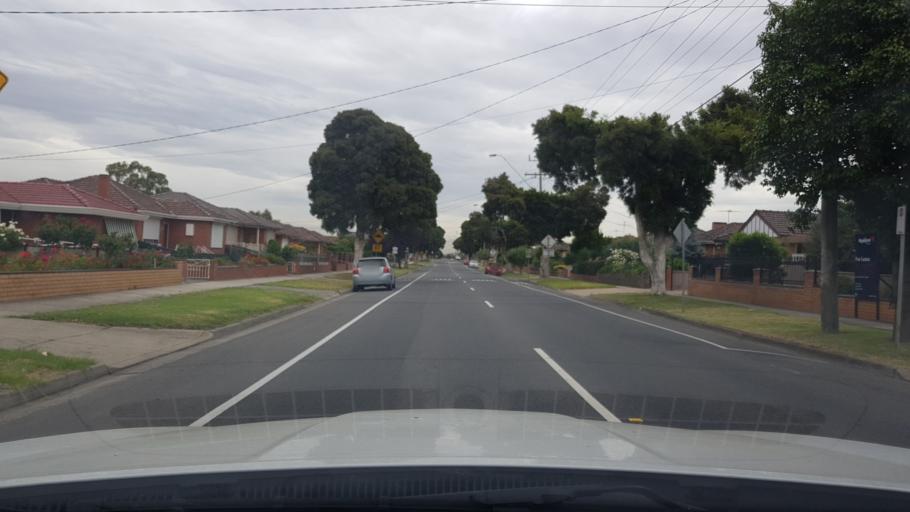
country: AU
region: Victoria
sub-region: Whittlesea
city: Lalor
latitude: -37.6651
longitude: 145.0124
